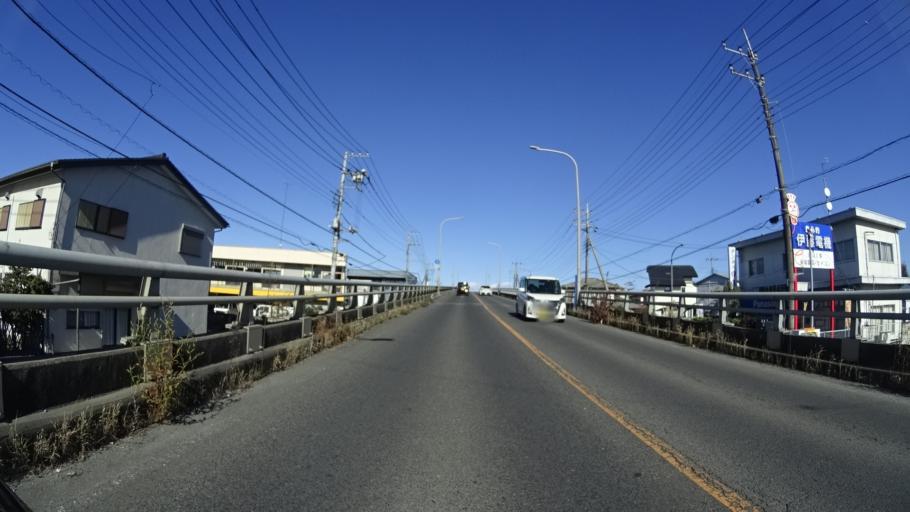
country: JP
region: Tochigi
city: Tochigi
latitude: 36.3989
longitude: 139.7383
